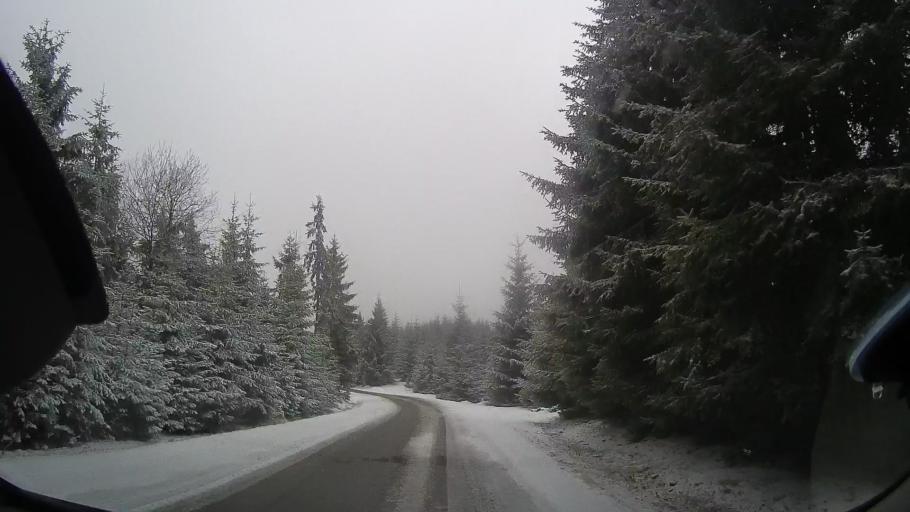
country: RO
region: Cluj
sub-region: Comuna Belis
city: Belis
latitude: 46.6441
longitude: 23.0693
